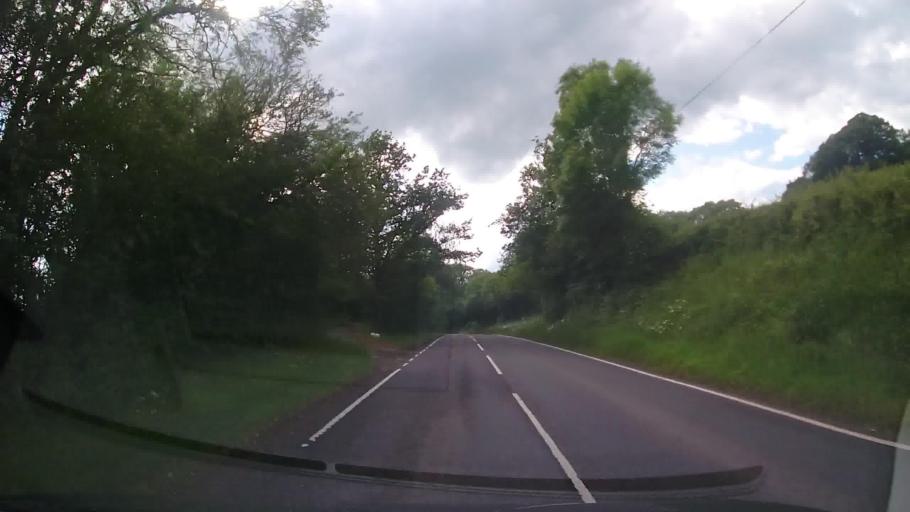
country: GB
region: England
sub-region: Shropshire
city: Much Wenlock
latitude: 52.6410
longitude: -2.5459
